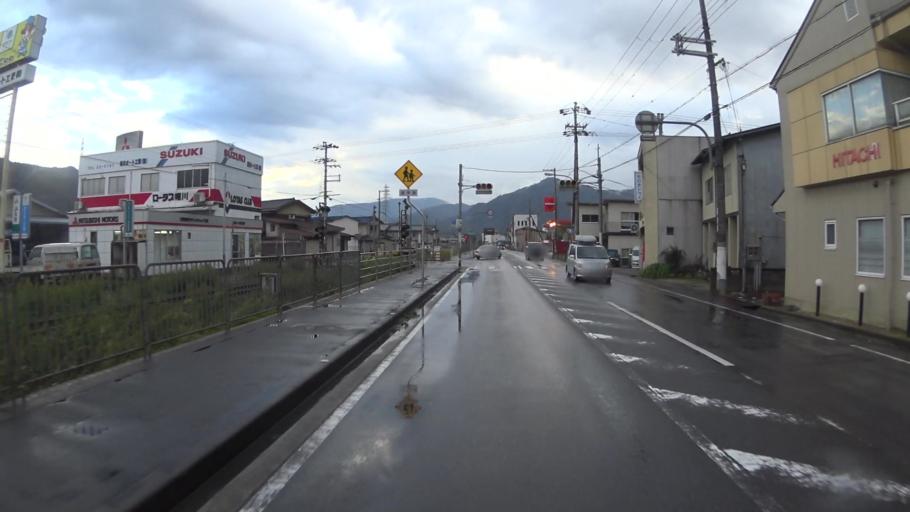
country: JP
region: Kyoto
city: Miyazu
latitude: 35.5385
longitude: 135.2059
